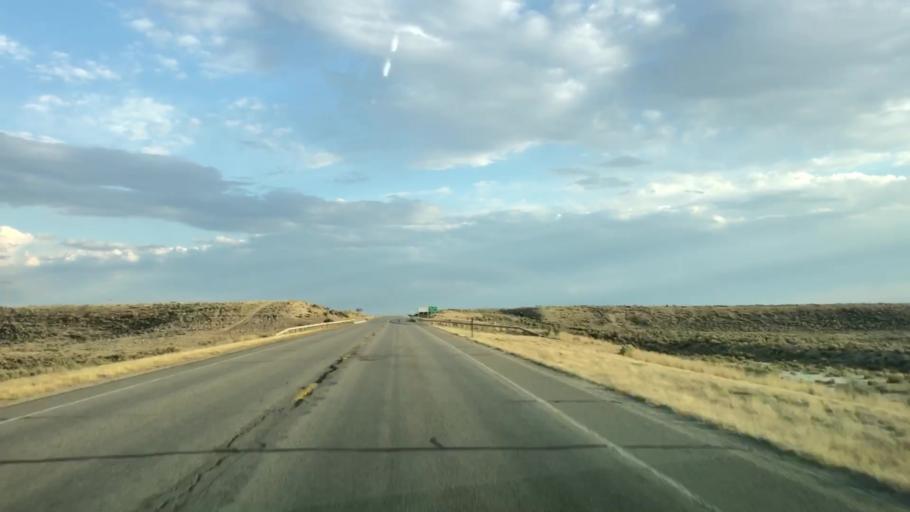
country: US
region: Wyoming
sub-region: Sweetwater County
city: North Rock Springs
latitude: 42.1011
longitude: -109.4462
